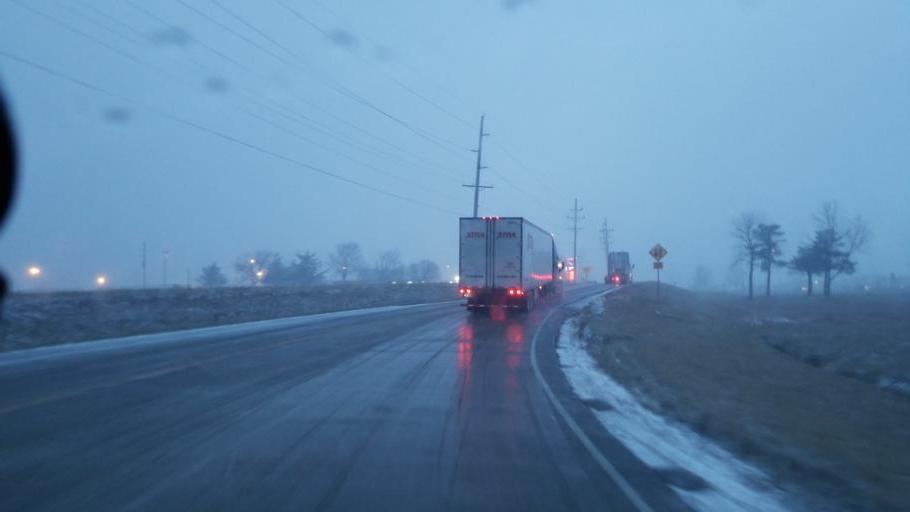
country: US
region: Missouri
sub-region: Warren County
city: Warrenton
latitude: 38.8379
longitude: -91.2269
